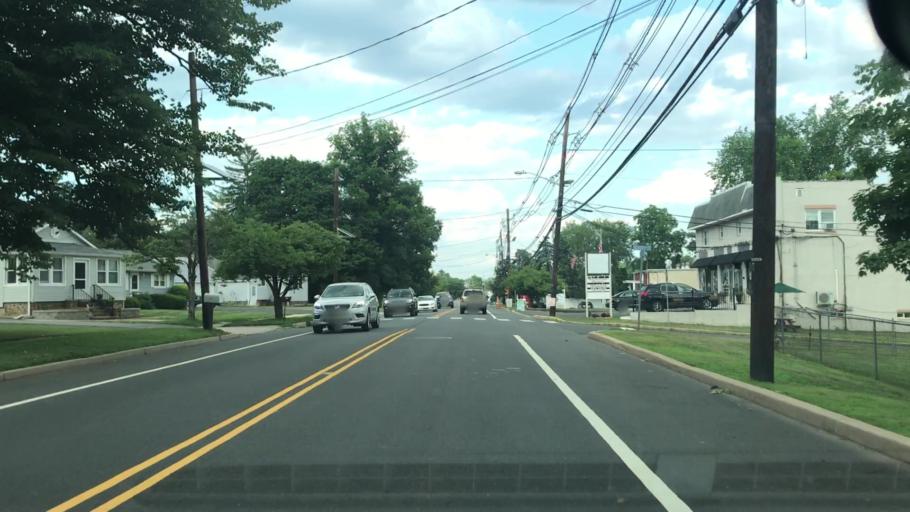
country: US
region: New Jersey
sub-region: Somerset County
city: Bradley Gardens
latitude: 40.5580
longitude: -74.6568
